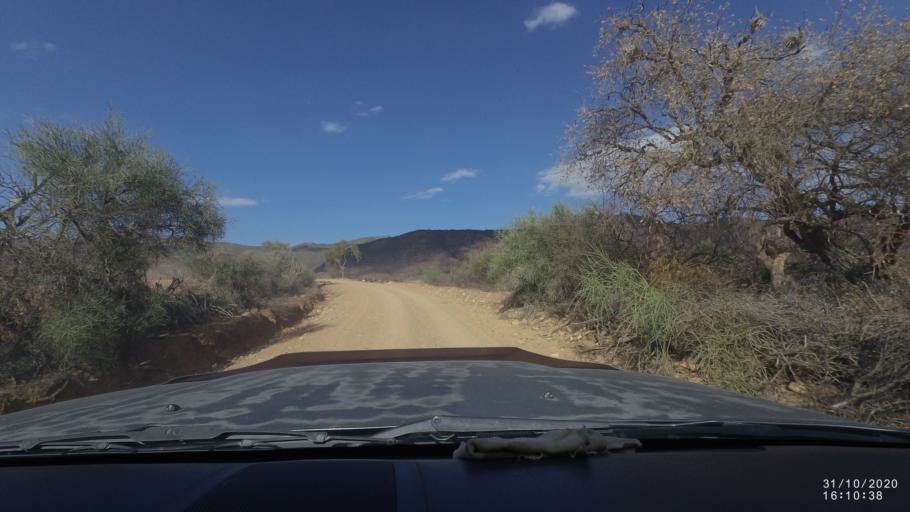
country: BO
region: Chuquisaca
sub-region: Provincia Zudanez
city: Mojocoya
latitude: -18.3832
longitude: -64.6282
